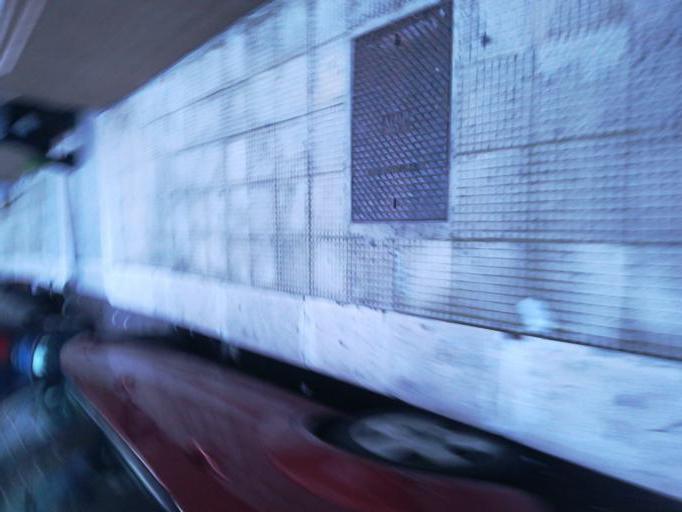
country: IT
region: Apulia
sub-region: Provincia di Bari
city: San Paolo
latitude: 41.1218
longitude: 16.7826
